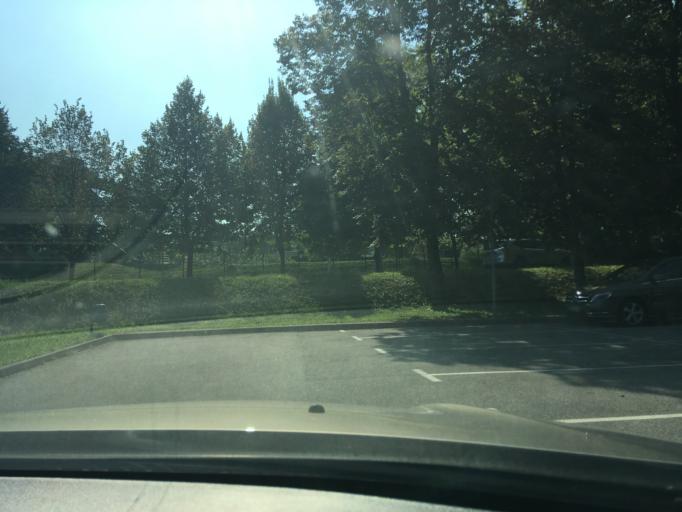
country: SI
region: Dolenjske Toplice
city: Dolenjske Toplice
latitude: 45.7599
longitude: 15.0565
